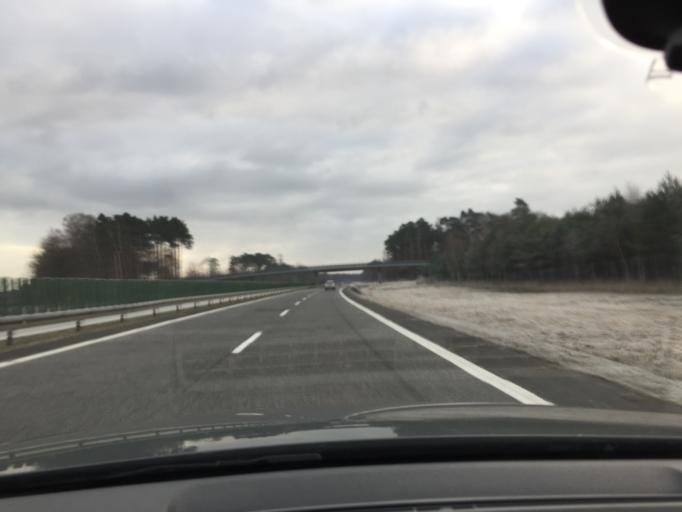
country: PL
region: Lubusz
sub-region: Powiat zarski
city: Lipinki Luzyckie
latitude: 51.6118
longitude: 14.9586
